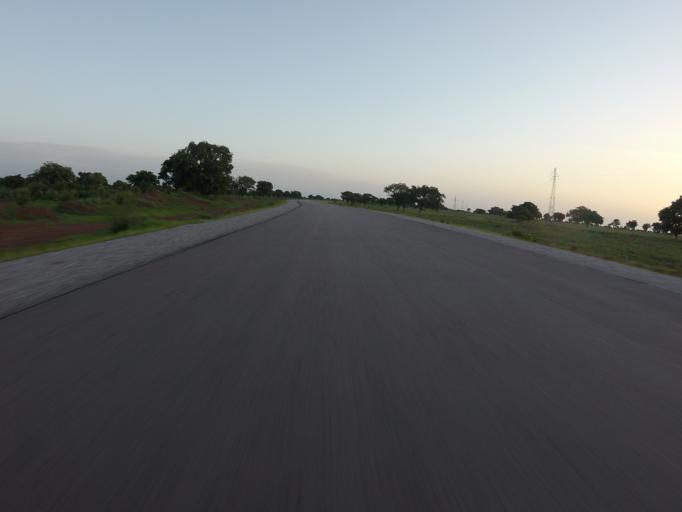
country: GH
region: Northern
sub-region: Yendi
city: Yendi
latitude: 9.9563
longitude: -0.1512
